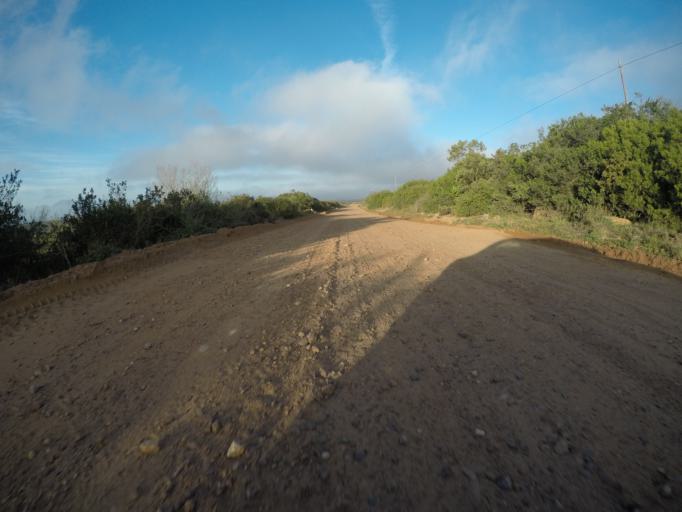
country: ZA
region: Western Cape
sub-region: Eden District Municipality
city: Mossel Bay
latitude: -34.1439
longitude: 22.0222
